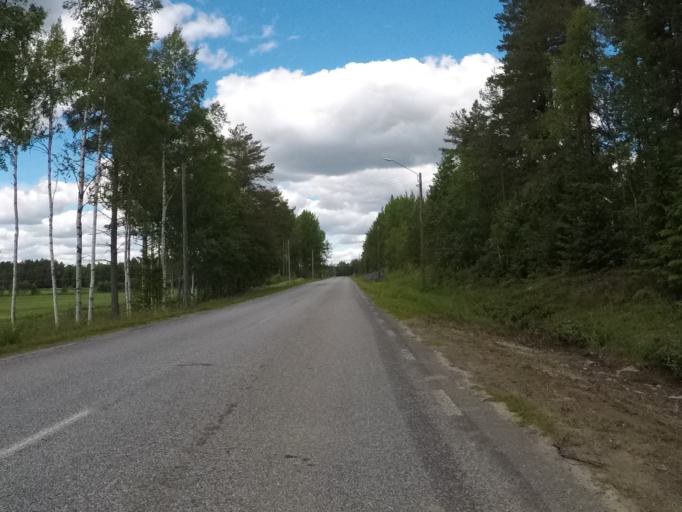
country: SE
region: Vaesterbotten
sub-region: Robertsfors Kommun
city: Robertsfors
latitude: 63.9942
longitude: 20.8085
